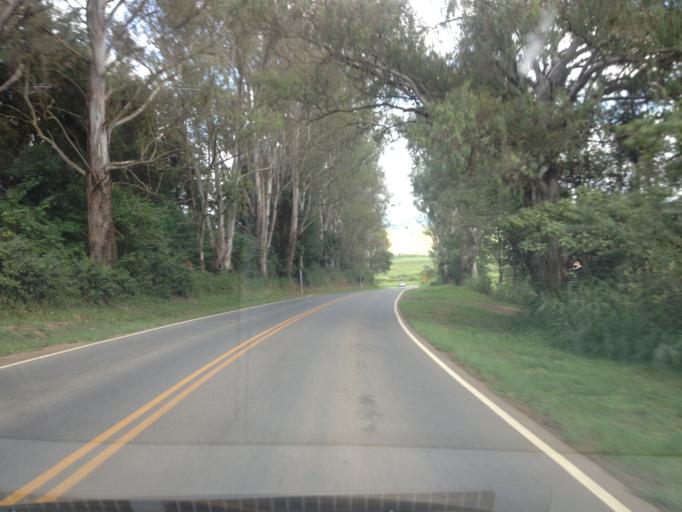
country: BR
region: Minas Gerais
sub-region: Itanhandu
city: Itanhandu
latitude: -22.2339
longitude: -44.9340
